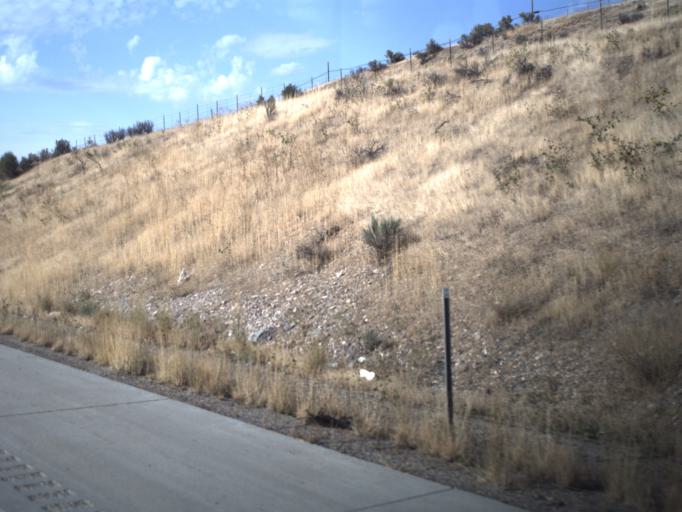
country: US
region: Utah
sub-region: Morgan County
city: Morgan
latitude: 41.0863
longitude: -111.7328
